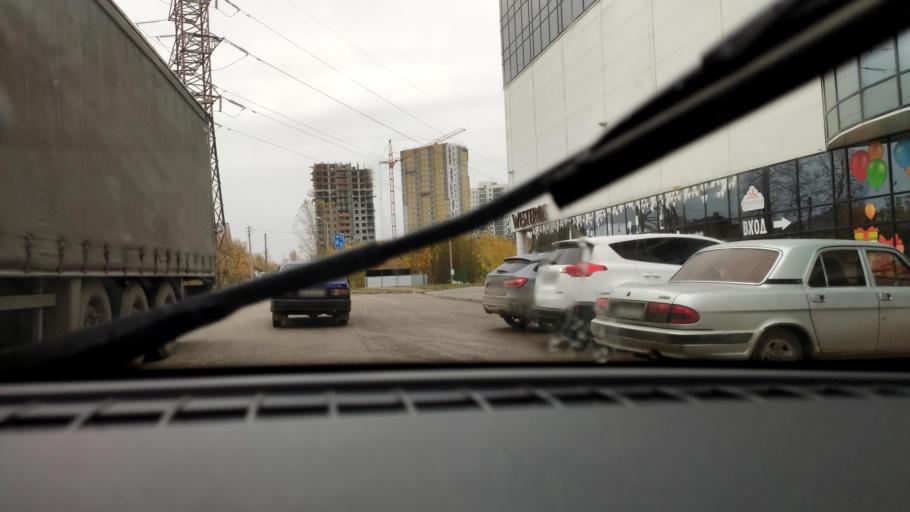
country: RU
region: Perm
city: Perm
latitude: 57.9766
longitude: 56.1905
